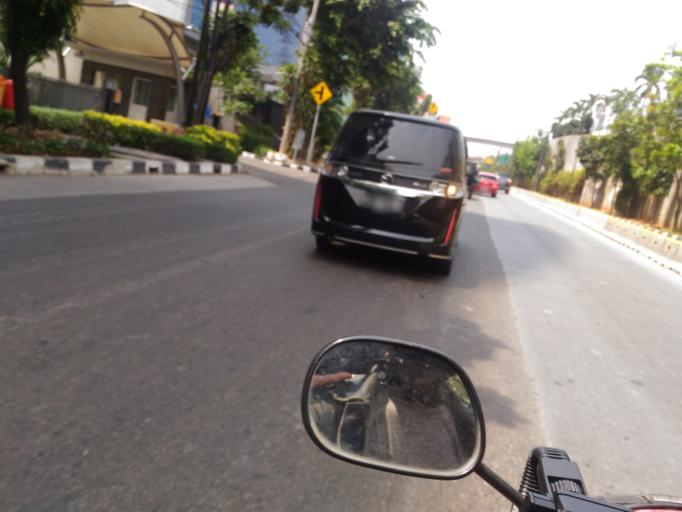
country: ID
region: Jakarta Raya
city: Jakarta
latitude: -6.2422
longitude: 106.8768
